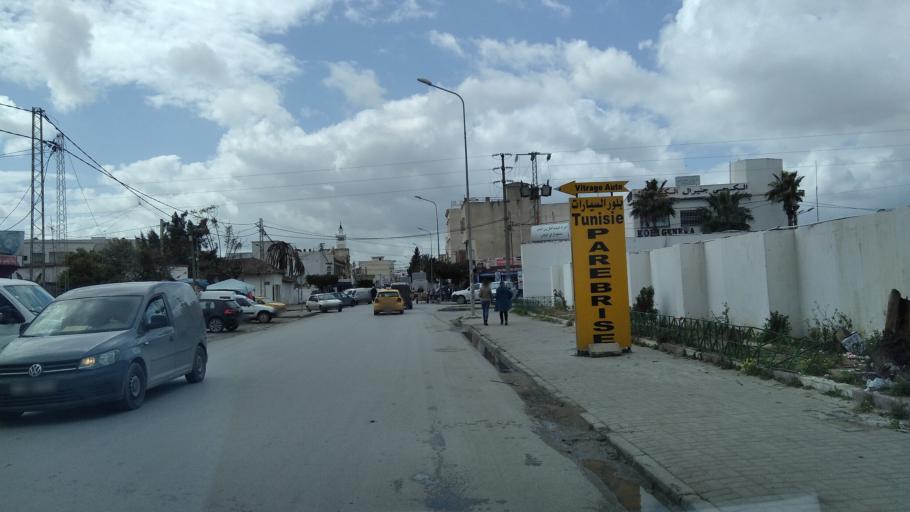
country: TN
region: Bin 'Arus
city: Ben Arous
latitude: 36.7601
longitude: 10.2236
